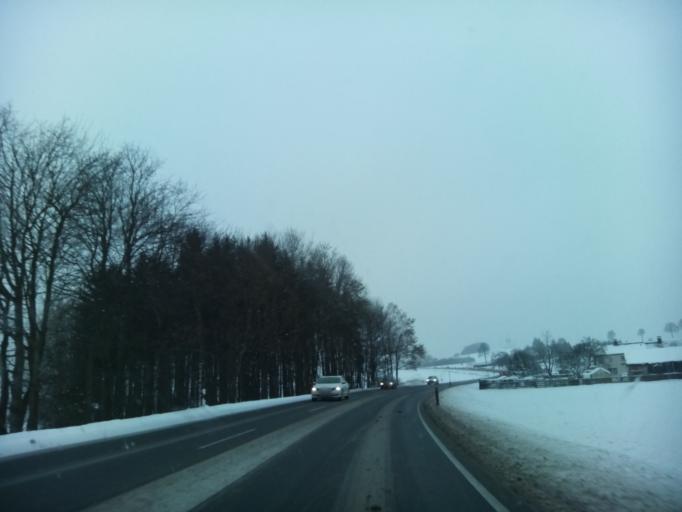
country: DE
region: Saxony
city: Grossolbersdorf
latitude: 50.7153
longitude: 13.0997
